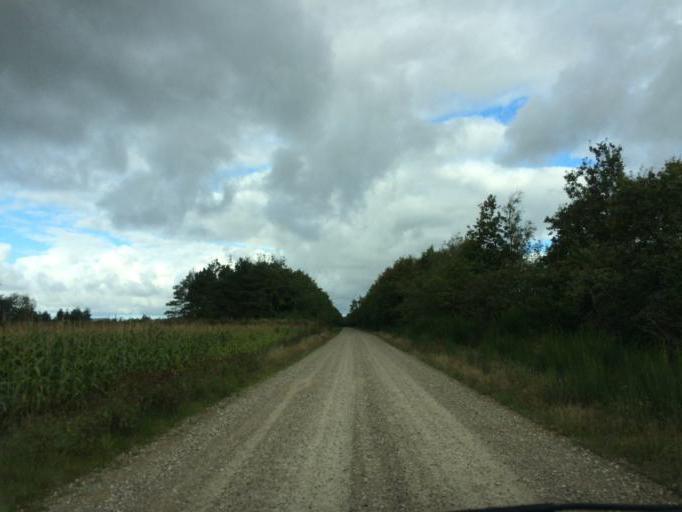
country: DK
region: Central Jutland
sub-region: Holstebro Kommune
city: Ulfborg
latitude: 56.2859
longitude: 8.3885
